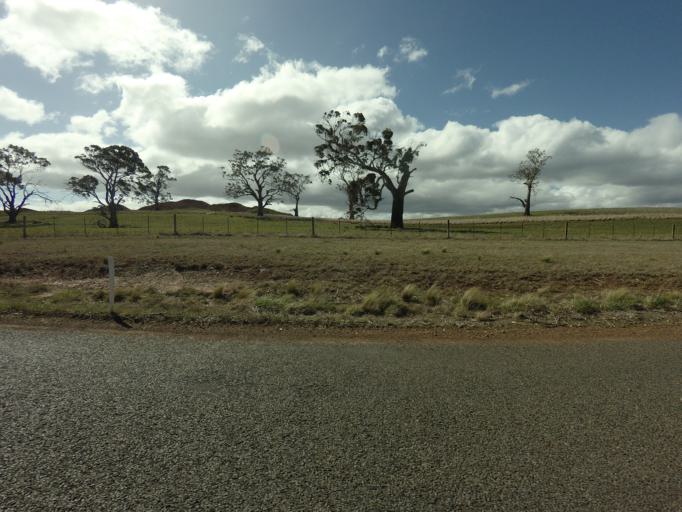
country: AU
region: Tasmania
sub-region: Northern Midlands
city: Evandale
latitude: -41.9068
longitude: 147.4569
